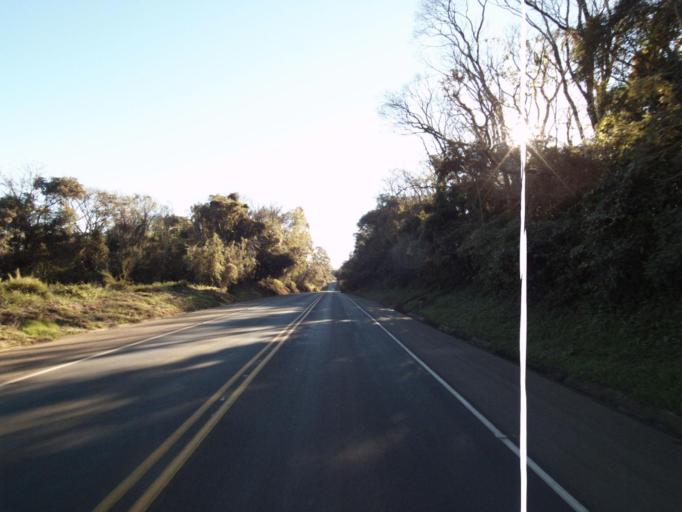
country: BR
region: Santa Catarina
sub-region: Chapeco
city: Chapeco
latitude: -27.0006
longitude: -52.7117
